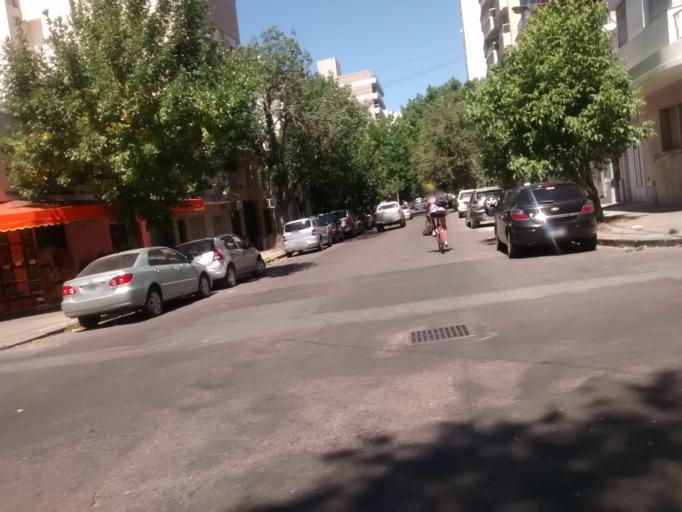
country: AR
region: Buenos Aires
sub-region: Partido de La Plata
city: La Plata
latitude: -34.9136
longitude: -57.9424
